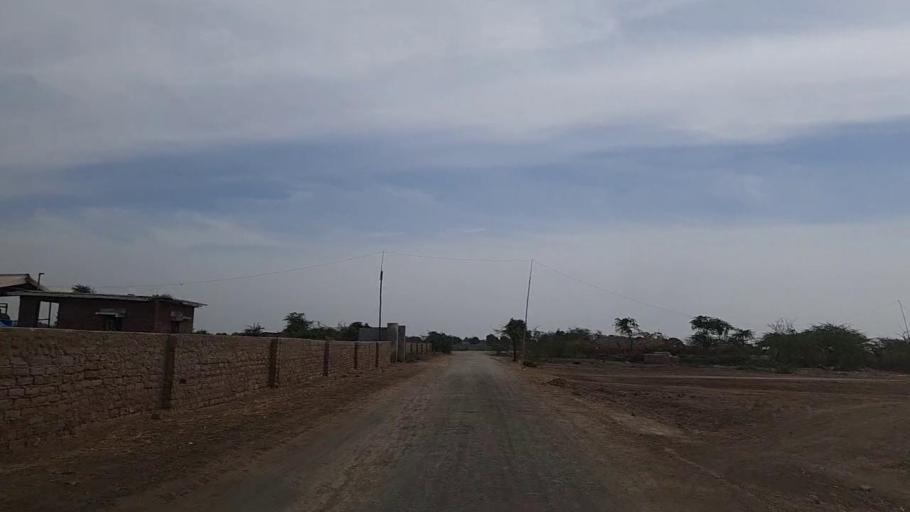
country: PK
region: Sindh
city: Samaro
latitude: 25.3053
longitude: 69.4515
